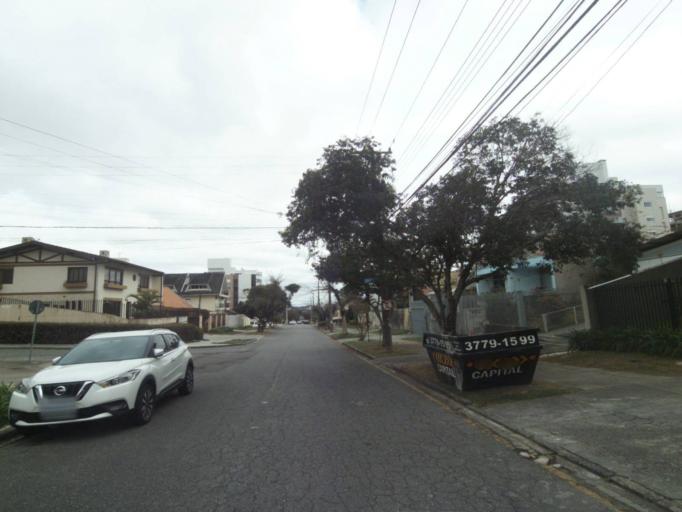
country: BR
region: Parana
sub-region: Curitiba
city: Curitiba
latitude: -25.4628
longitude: -49.2920
